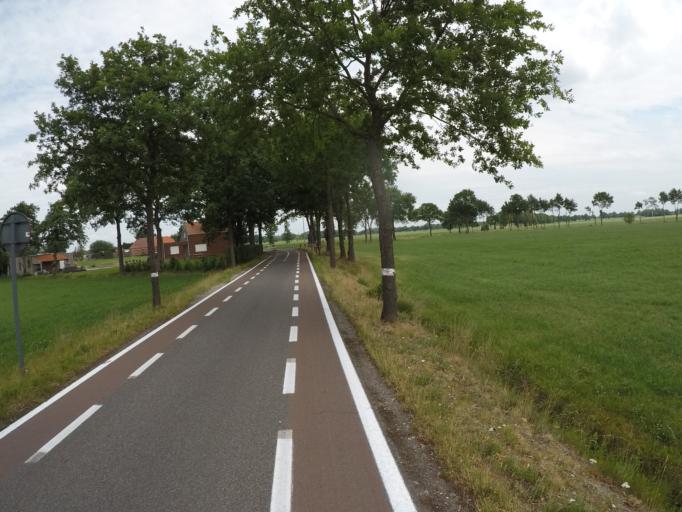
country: BE
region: Flanders
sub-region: Provincie Antwerpen
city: Kalmthout
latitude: 51.4162
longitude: 4.5025
